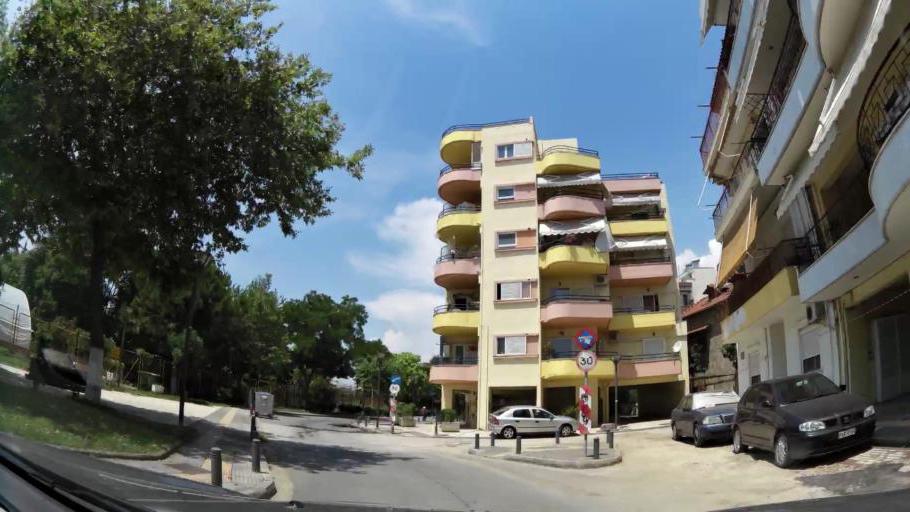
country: GR
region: Central Macedonia
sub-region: Nomos Thessalonikis
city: Ampelokipoi
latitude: 40.6548
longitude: 22.9164
